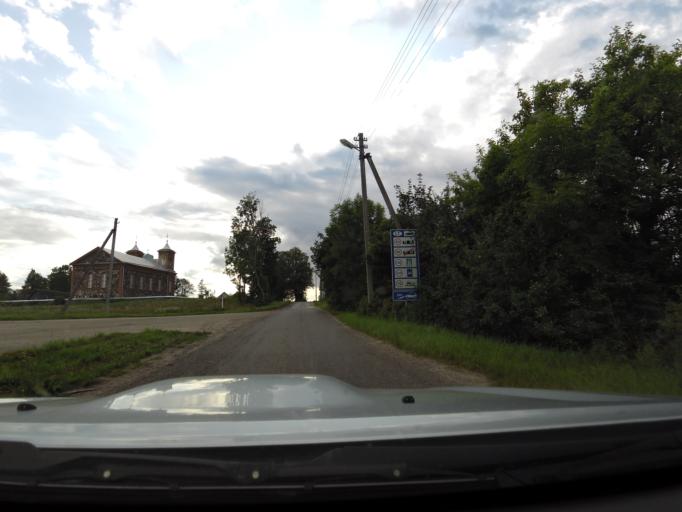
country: LV
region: Nereta
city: Nereta
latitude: 56.1603
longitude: 25.2785
